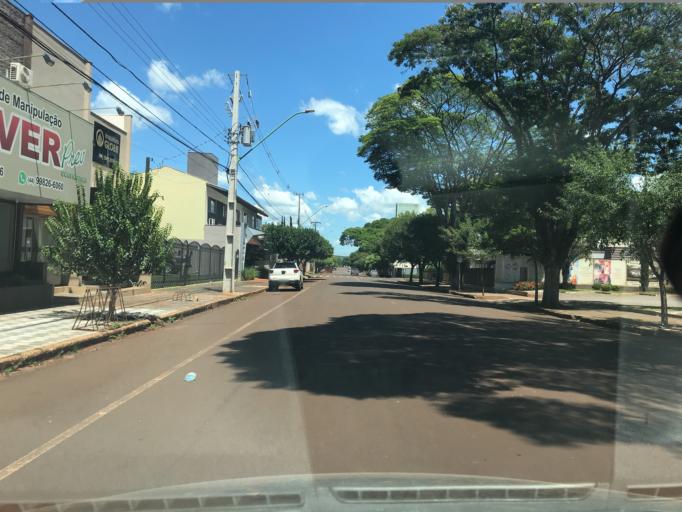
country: BR
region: Parana
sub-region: Palotina
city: Palotina
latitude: -24.2847
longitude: -53.8411
